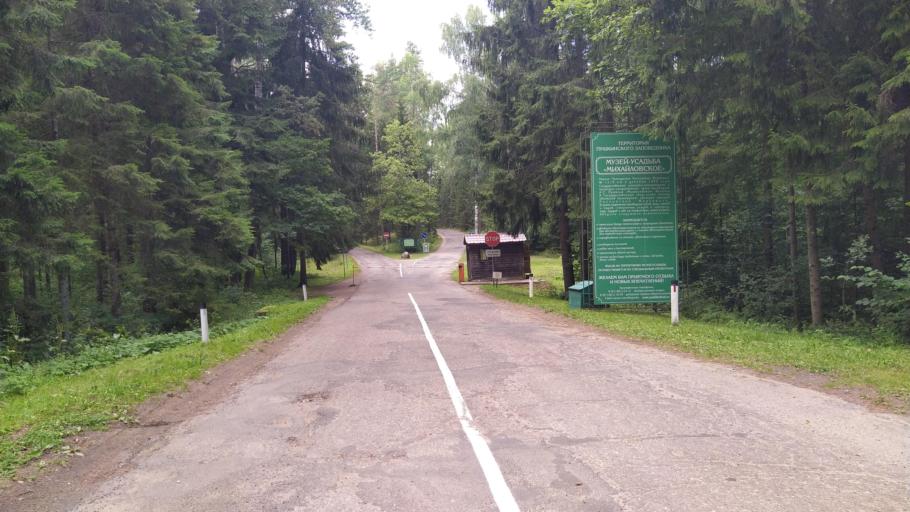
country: RU
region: Pskov
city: Pushkinskiye Gory
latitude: 57.0572
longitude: 28.9454
